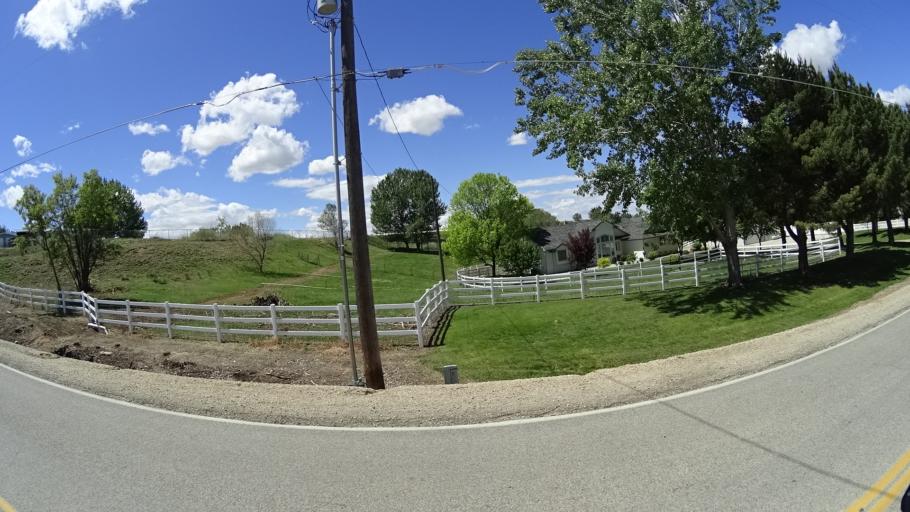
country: US
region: Idaho
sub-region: Ada County
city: Meridian
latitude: 43.5936
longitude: -116.4735
